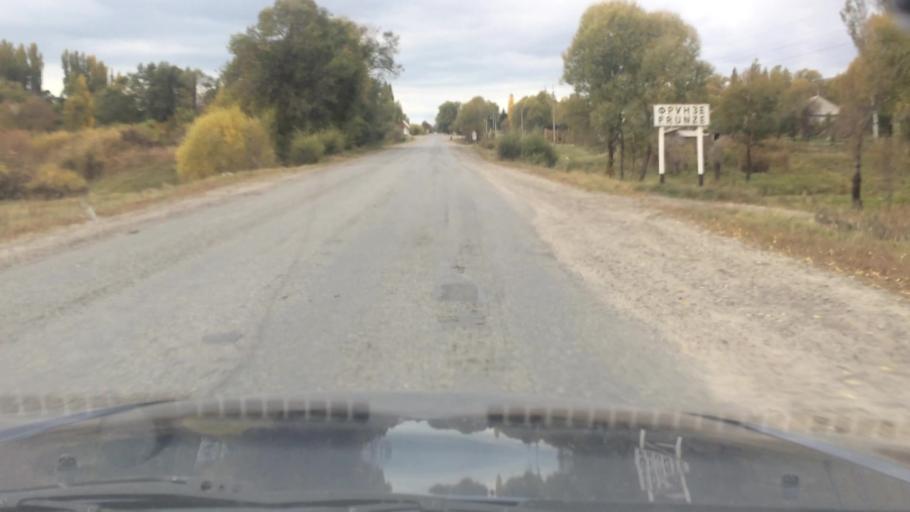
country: KG
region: Ysyk-Koel
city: Tyup
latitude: 42.7698
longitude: 78.1895
